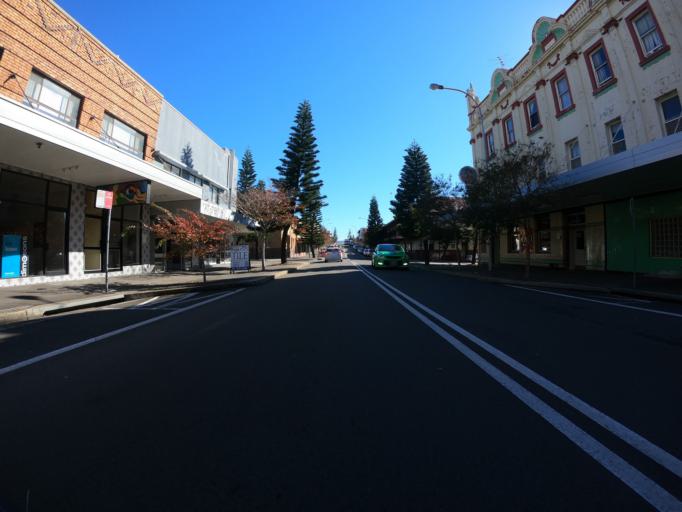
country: AU
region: New South Wales
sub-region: Wollongong
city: Port Kembla
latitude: -34.4815
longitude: 150.9021
